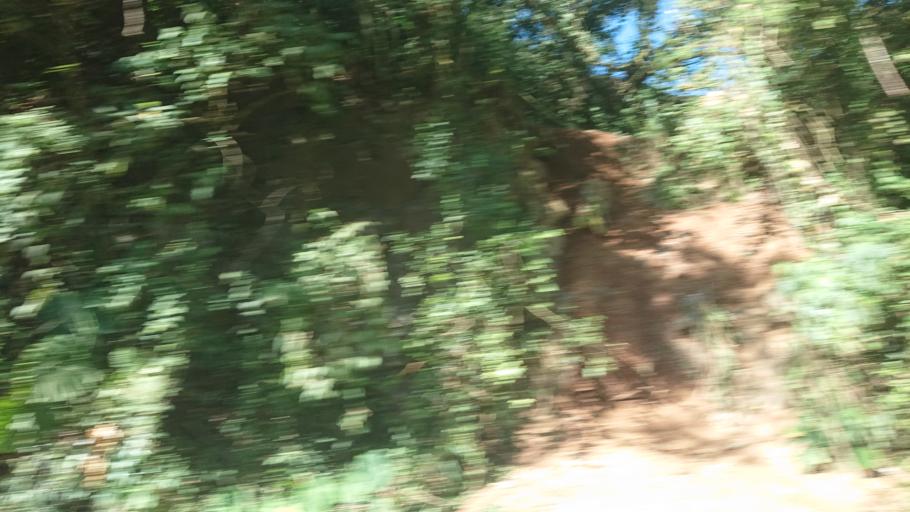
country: TW
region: Taiwan
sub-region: Chiayi
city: Jiayi Shi
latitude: 23.4761
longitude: 120.7123
